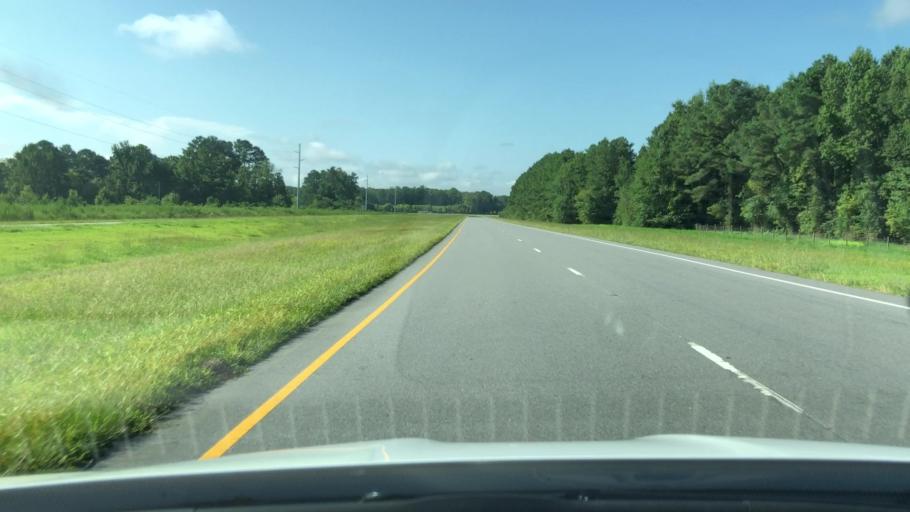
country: US
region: North Carolina
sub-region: Pasquotank County
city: Elizabeth City
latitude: 36.4419
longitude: -76.3392
